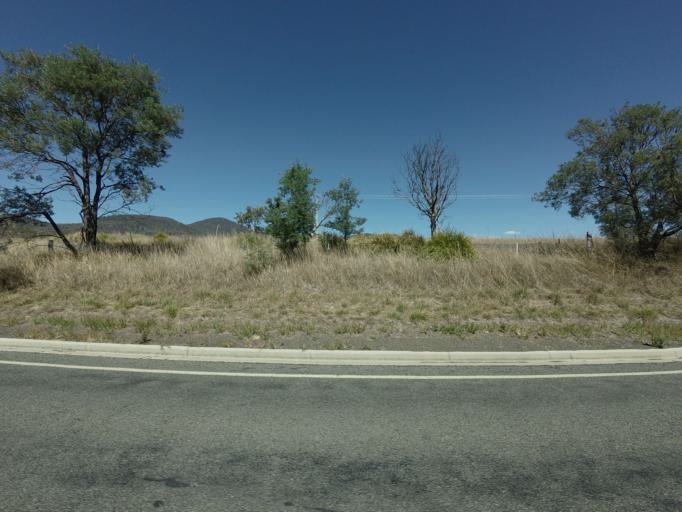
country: AU
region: Tasmania
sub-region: Northern Midlands
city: Evandale
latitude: -41.7393
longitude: 147.7962
